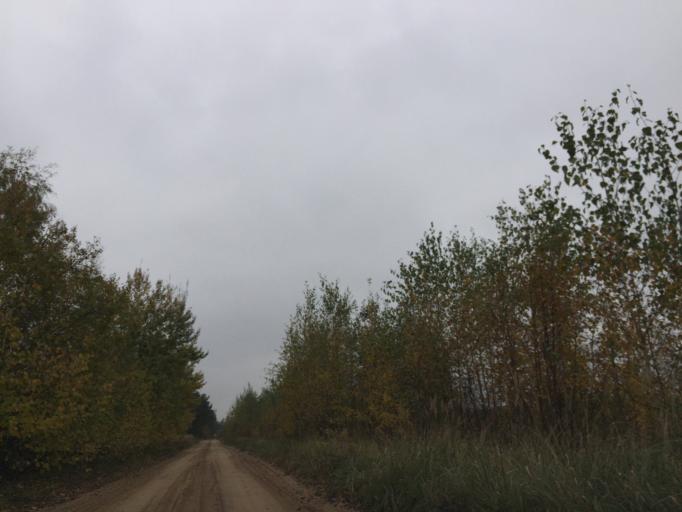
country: LV
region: Dobeles Rajons
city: Dobele
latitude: 56.6737
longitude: 23.4602
